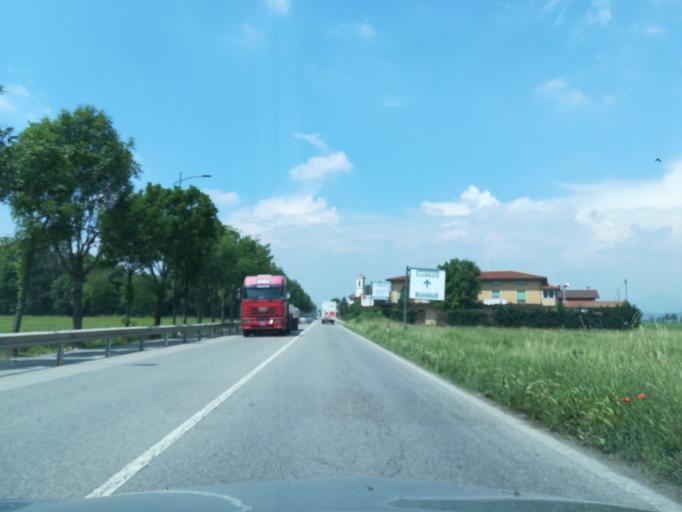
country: IT
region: Lombardy
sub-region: Provincia di Bergamo
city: Cavernago
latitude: 45.6273
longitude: 9.7680
